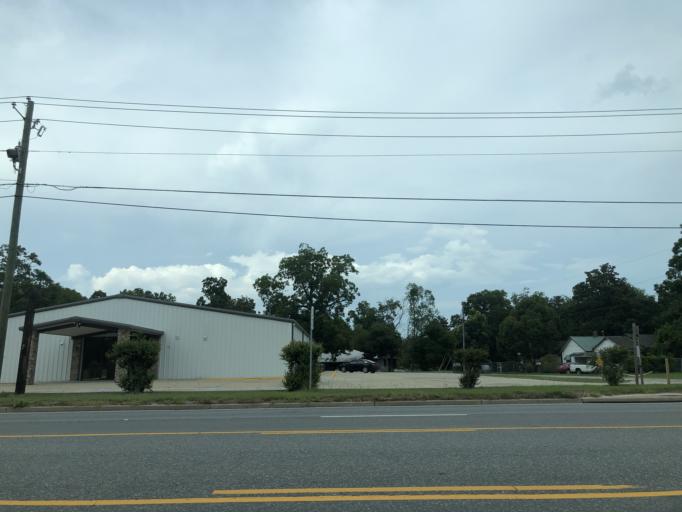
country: US
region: Georgia
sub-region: Wayne County
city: Jesup
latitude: 31.6048
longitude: -81.8778
